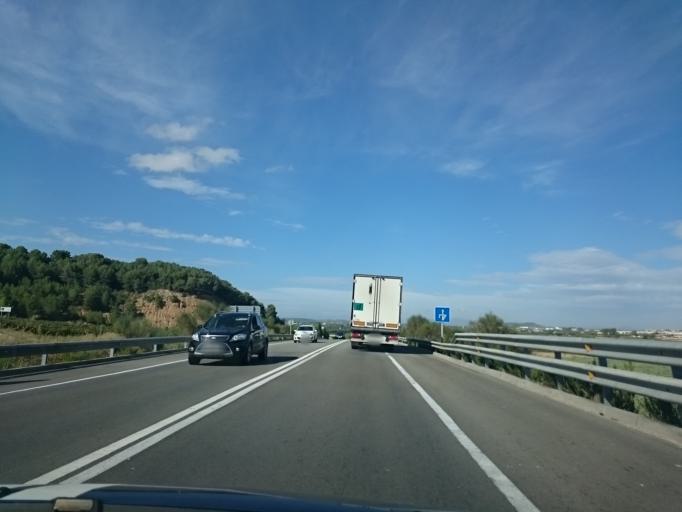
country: ES
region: Catalonia
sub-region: Provincia de Barcelona
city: Castellet
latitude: 41.2998
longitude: 1.6332
